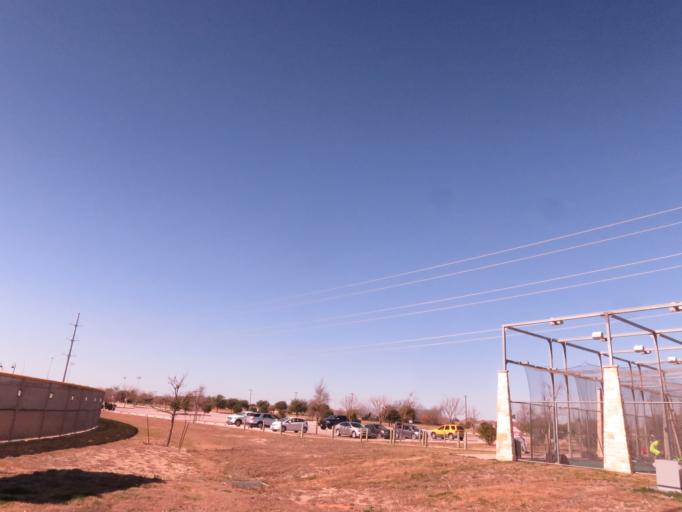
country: US
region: Texas
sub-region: Williamson County
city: Hutto
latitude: 30.5451
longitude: -97.6155
